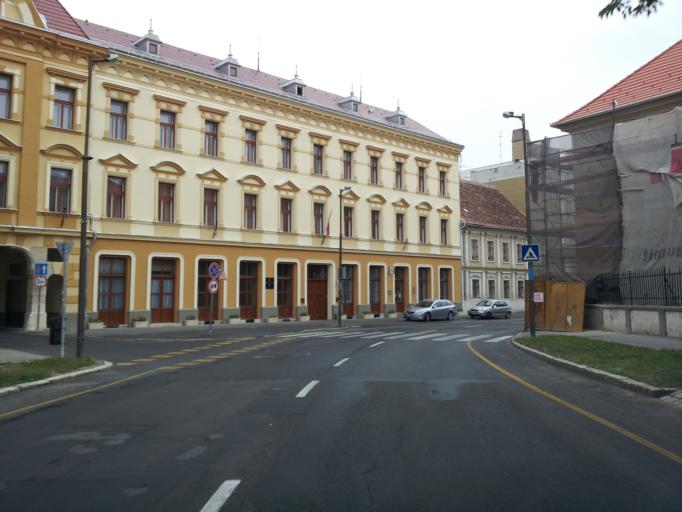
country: HU
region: Vas
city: Szombathely
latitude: 47.2306
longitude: 16.6186
